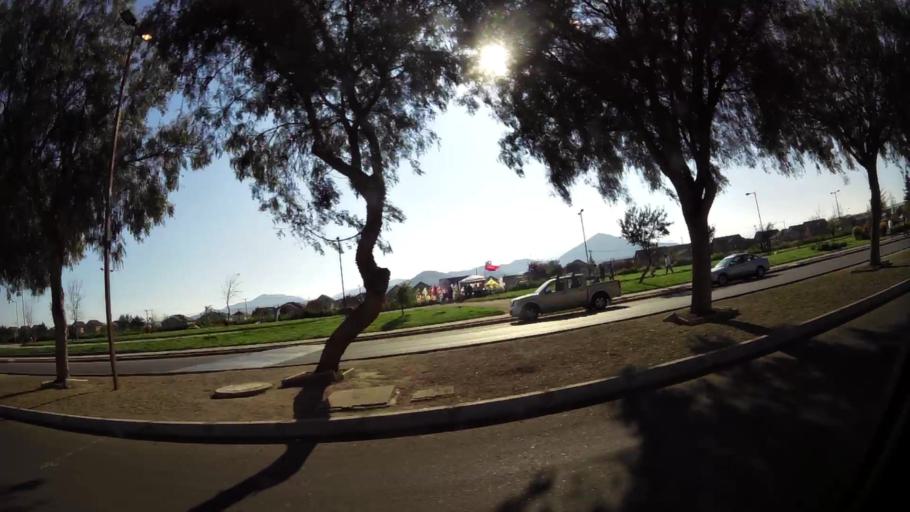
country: CL
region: Santiago Metropolitan
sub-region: Provincia de Santiago
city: Lo Prado
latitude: -33.4931
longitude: -70.7795
